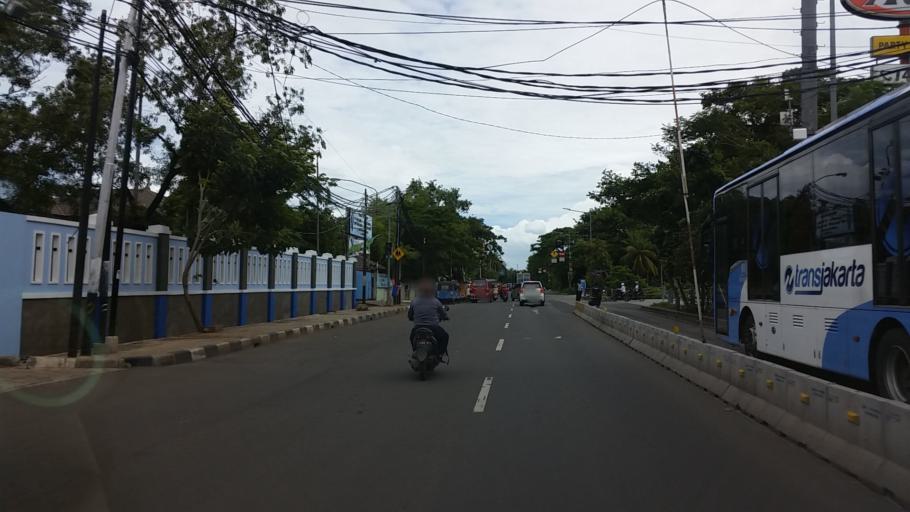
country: ID
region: Jakarta Raya
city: Jakarta
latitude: -6.1157
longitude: 106.7912
